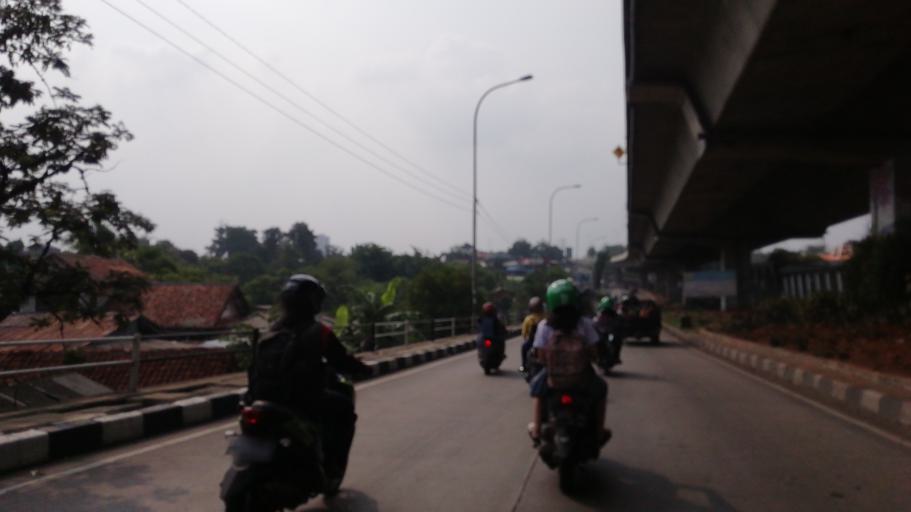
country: ID
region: West Java
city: Bogor
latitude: -6.5630
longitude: 106.8089
